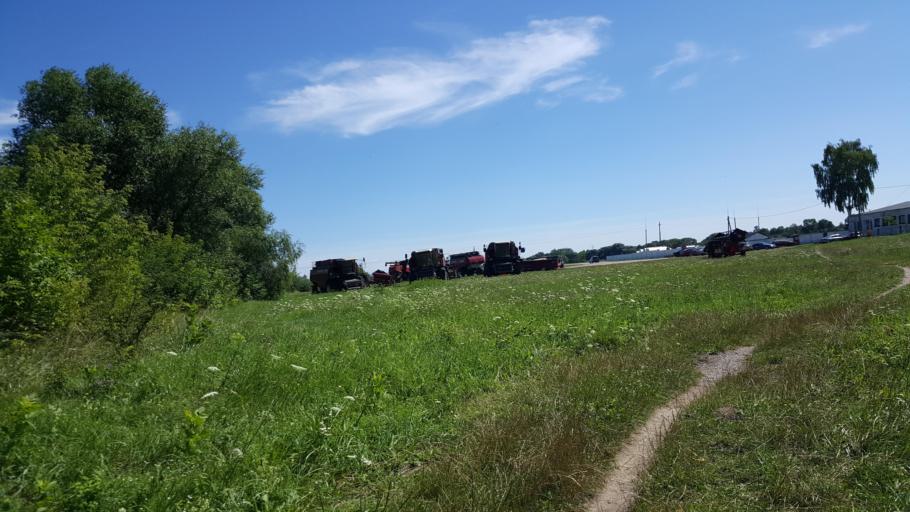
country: BY
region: Brest
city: Charnawchytsy
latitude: 52.2182
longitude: 23.7449
